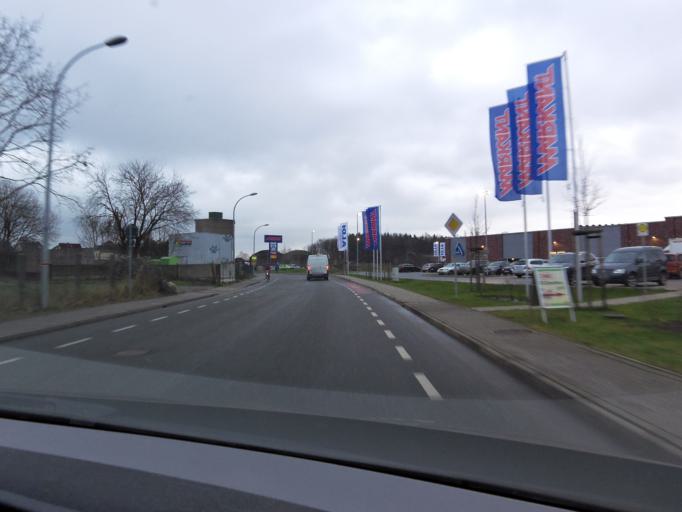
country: DE
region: Mecklenburg-Vorpommern
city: Grevesmuhlen
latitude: 53.8586
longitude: 11.1874
